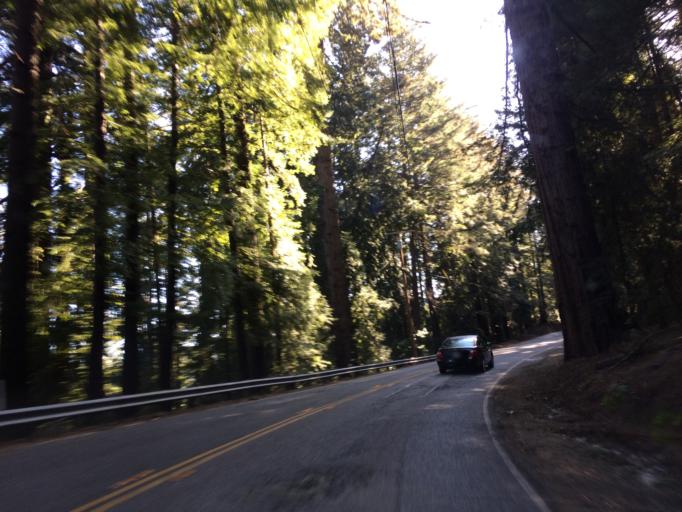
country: US
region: California
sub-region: Santa Clara County
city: Loyola
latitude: 37.2491
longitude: -122.1538
